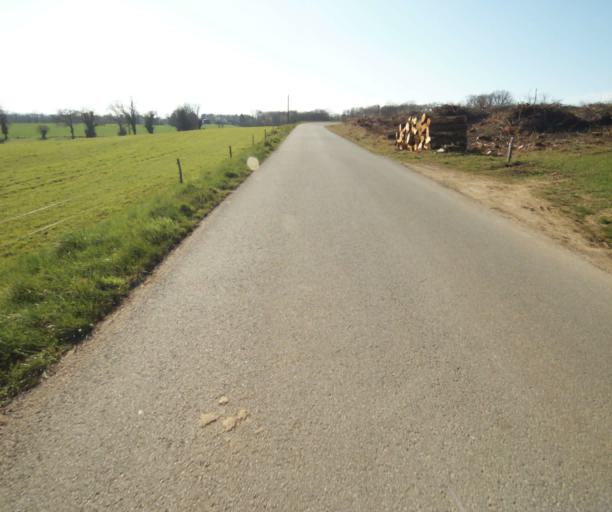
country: FR
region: Limousin
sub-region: Departement de la Correze
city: Chamboulive
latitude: 45.4763
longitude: 1.7168
